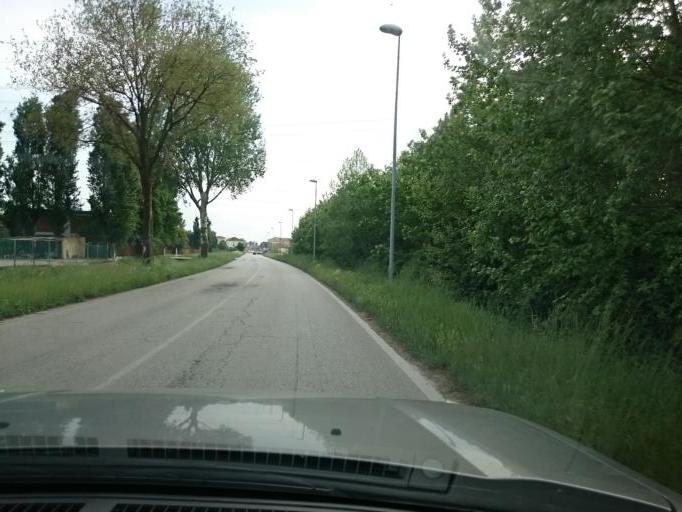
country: IT
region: Veneto
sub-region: Provincia di Venezia
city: Mestre
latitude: 45.4399
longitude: 12.2066
